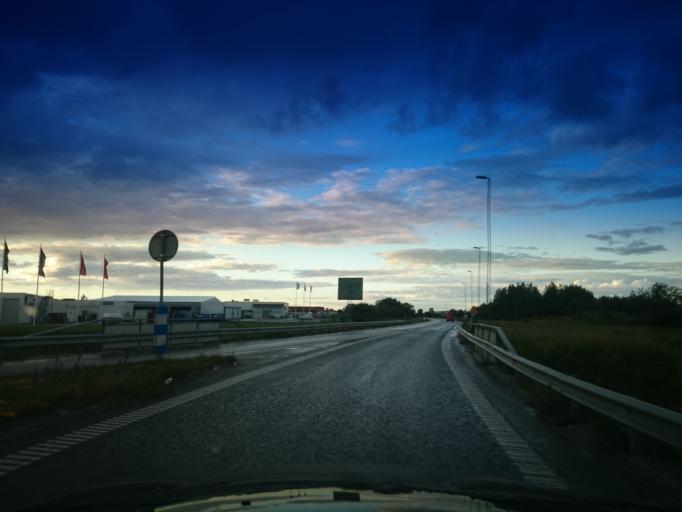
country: SE
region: Gotland
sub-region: Gotland
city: Visby
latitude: 57.6329
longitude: 18.3285
